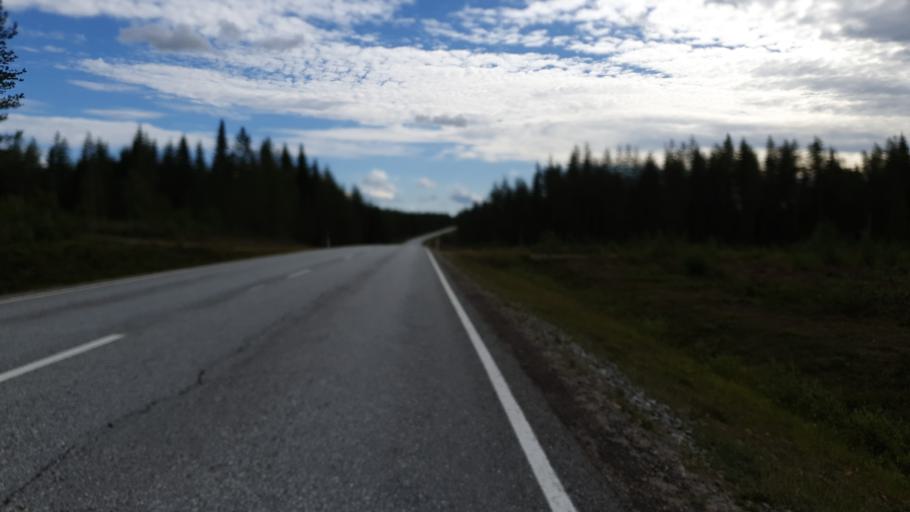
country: FI
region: Kainuu
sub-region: Kehys-Kainuu
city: Kuhmo
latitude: 64.4817
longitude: 29.7751
